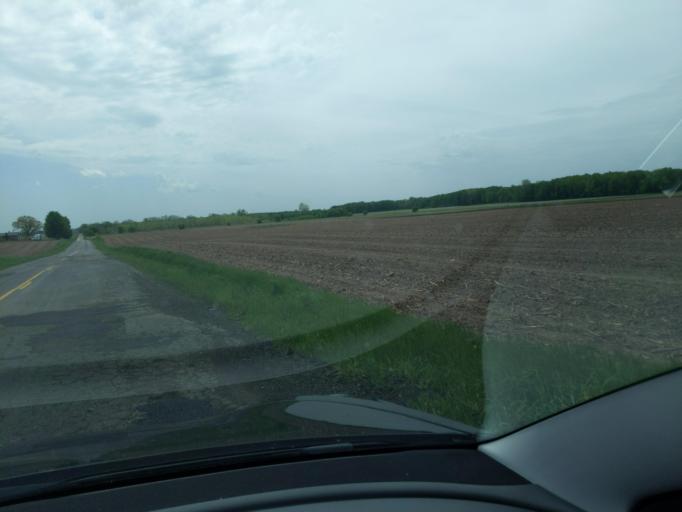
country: US
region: Michigan
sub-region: Ingham County
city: Holt
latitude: 42.5424
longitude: -84.5422
